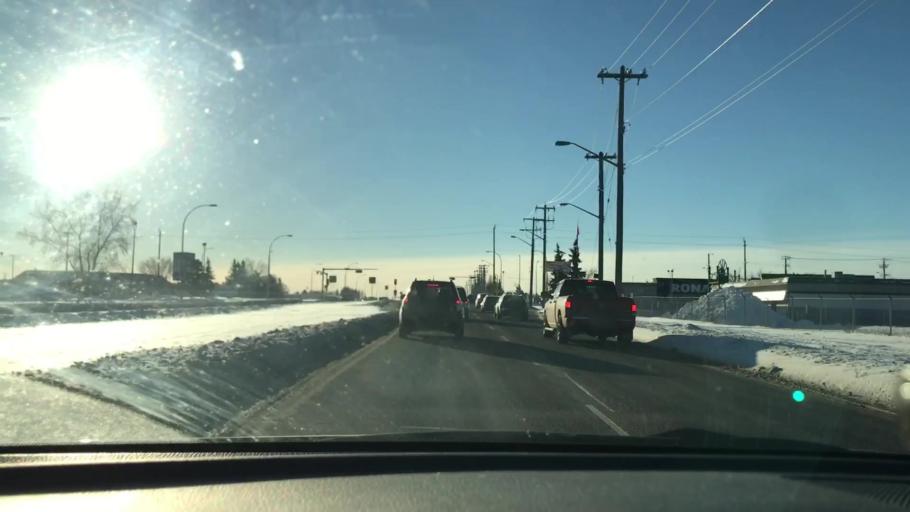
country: CA
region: Alberta
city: Edmonton
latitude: 53.4897
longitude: -113.4673
